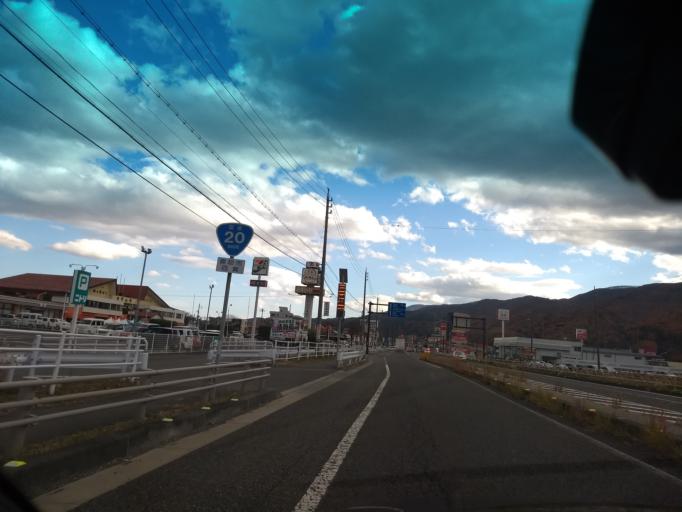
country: JP
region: Nagano
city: Chino
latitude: 36.0071
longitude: 138.1307
